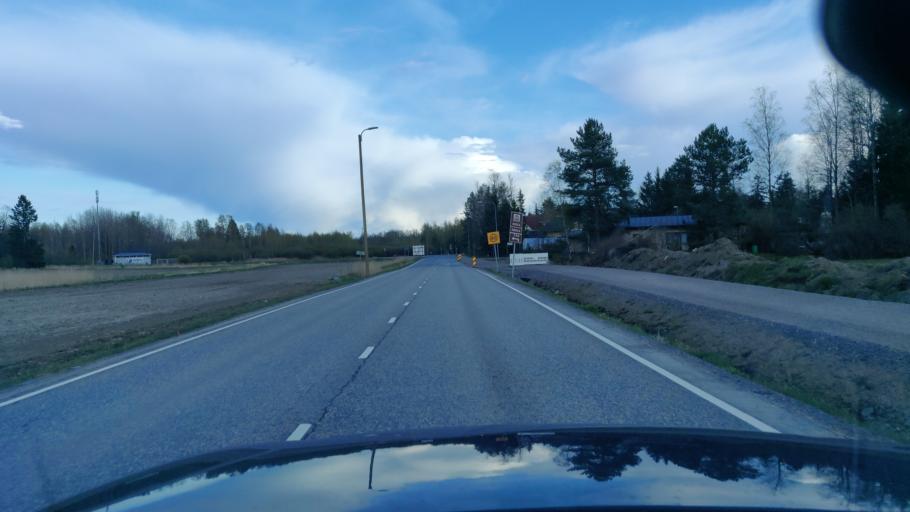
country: FI
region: Uusimaa
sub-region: Helsinki
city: Jaervenpaeae
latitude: 60.4710
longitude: 25.0698
